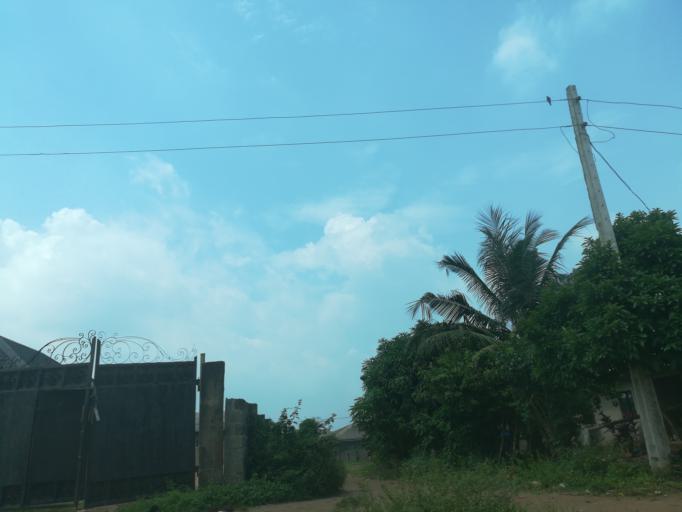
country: NG
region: Lagos
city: Ikorodu
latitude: 6.5998
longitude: 3.6261
